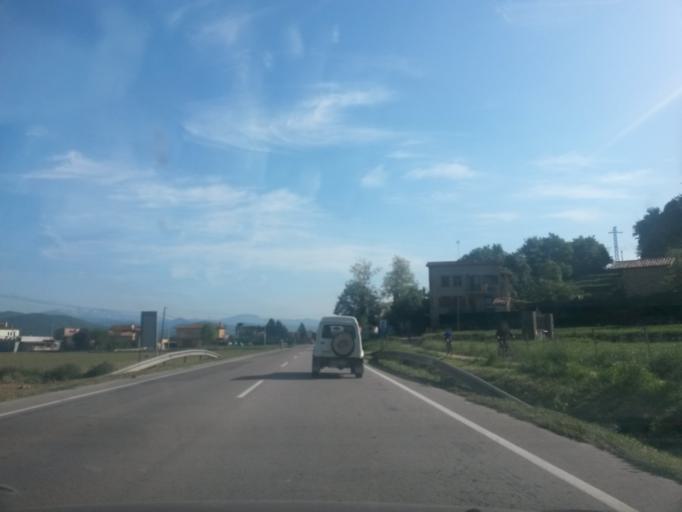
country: ES
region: Catalonia
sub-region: Provincia de Girona
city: Bas
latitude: 42.1375
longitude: 2.4548
